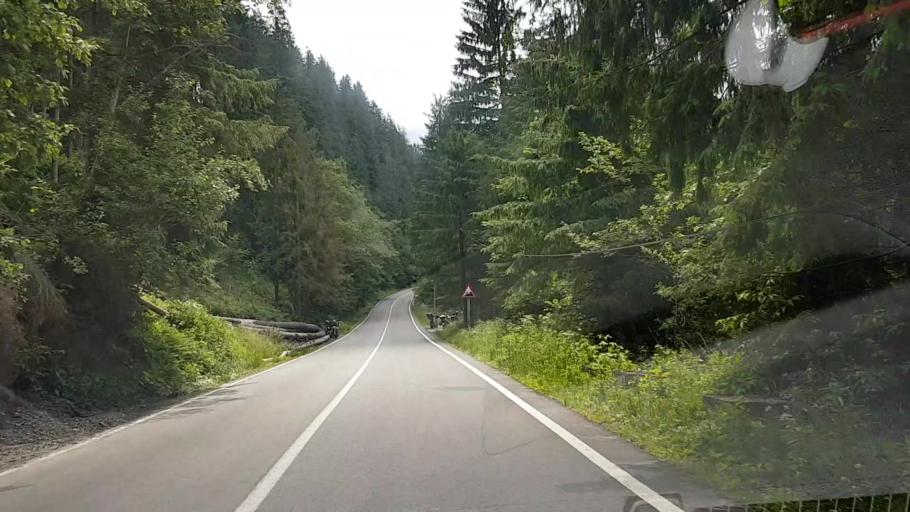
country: RO
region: Suceava
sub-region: Comuna Crucea
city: Crucea
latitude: 47.3653
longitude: 25.5915
